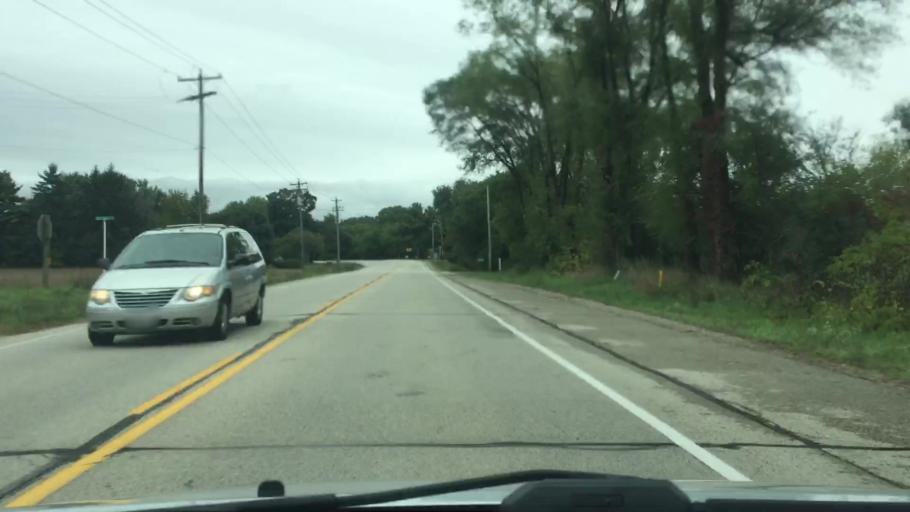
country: US
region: Wisconsin
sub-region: Jefferson County
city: Palmyra
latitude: 42.7907
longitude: -88.5631
